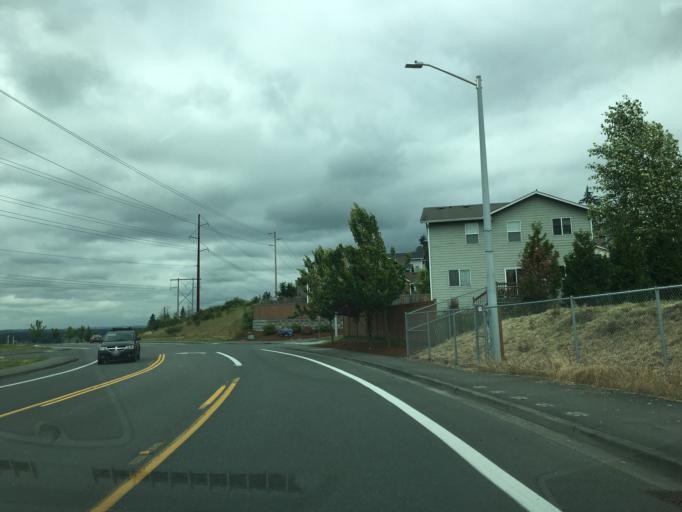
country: US
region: Washington
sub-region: Snohomish County
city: Sisco Heights
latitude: 48.0735
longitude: -122.1226
